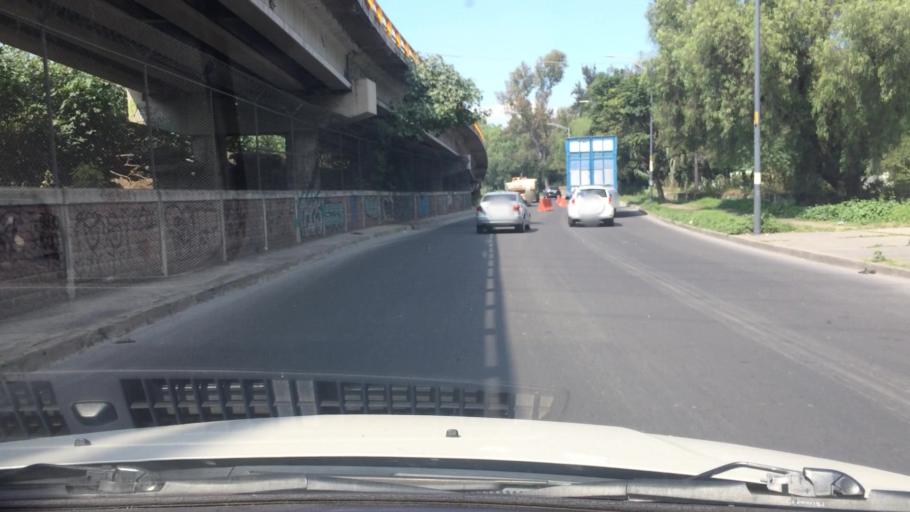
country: MX
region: Mexico
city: Colonia Lindavista
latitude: 19.5193
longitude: -99.1445
